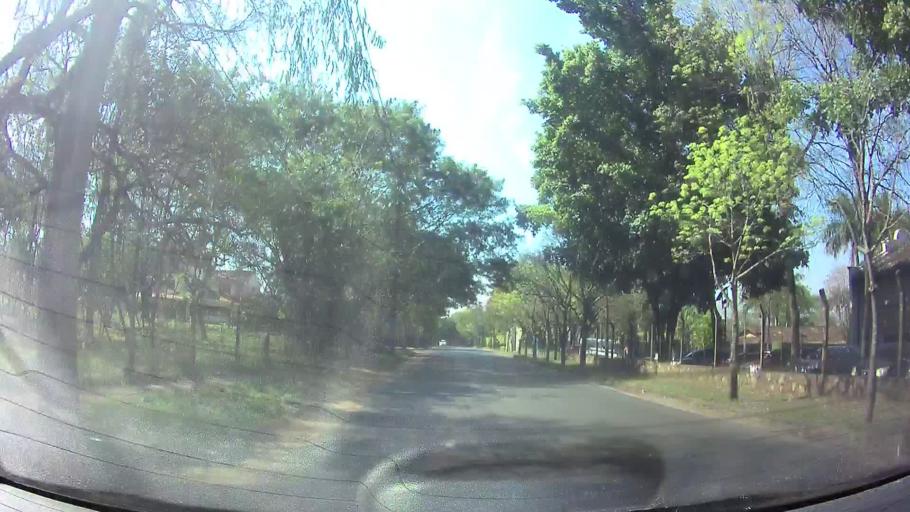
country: PY
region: Central
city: Fernando de la Mora
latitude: -25.2844
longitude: -57.5535
